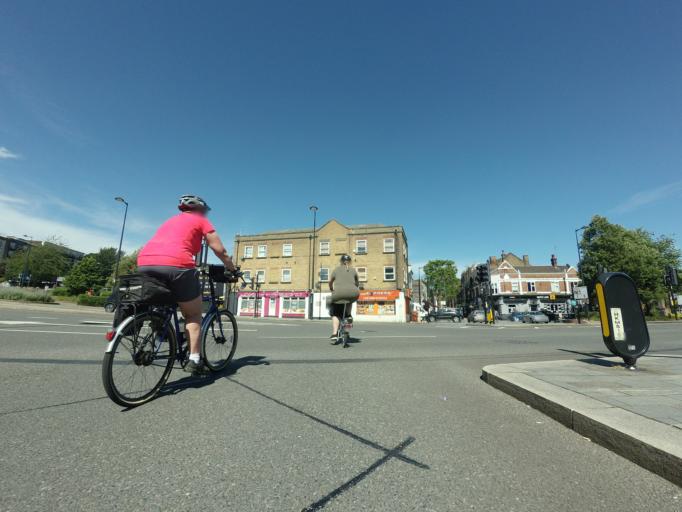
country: GB
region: England
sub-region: Kent
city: Chatham
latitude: 51.3801
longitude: 0.5304
